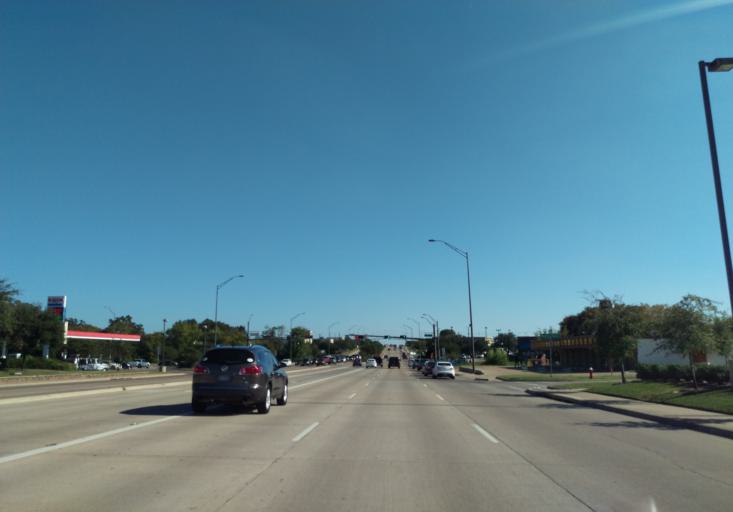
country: US
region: Texas
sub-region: Brazos County
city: College Station
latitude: 30.6159
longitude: -96.3203
